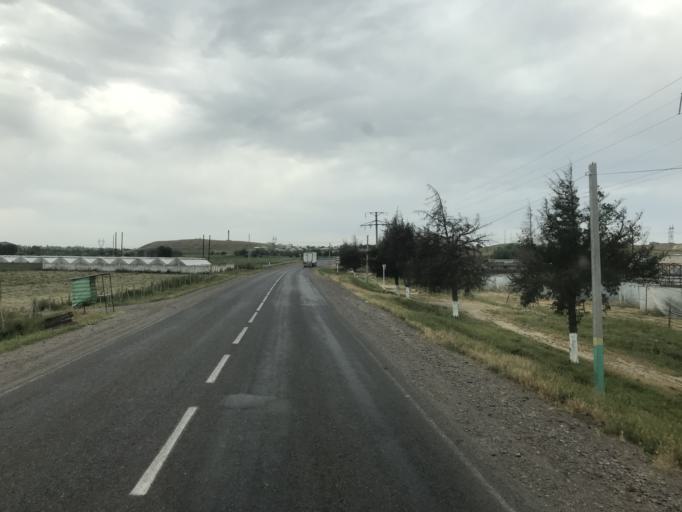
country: KZ
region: Ongtustik Qazaqstan
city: Saryaghash
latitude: 41.4843
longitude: 69.2540
